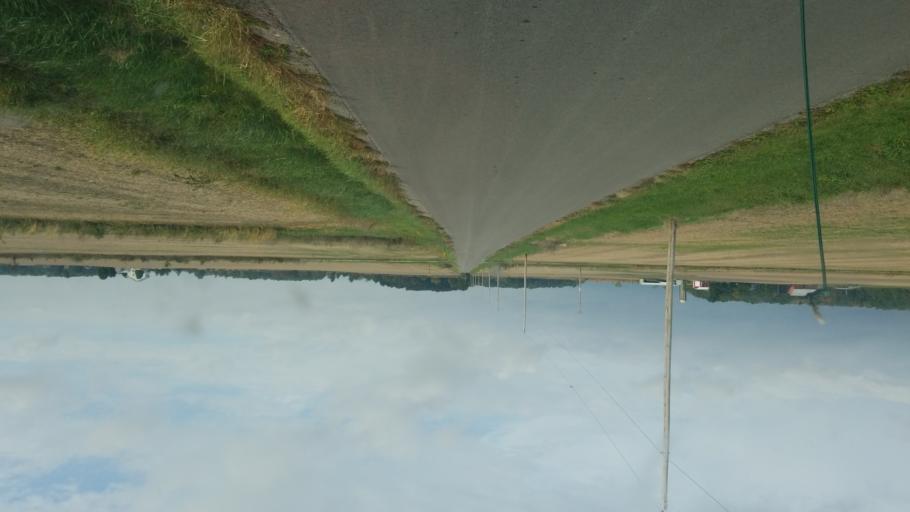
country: US
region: Ohio
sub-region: Wyandot County
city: Carey
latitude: 41.0269
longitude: -83.4486
